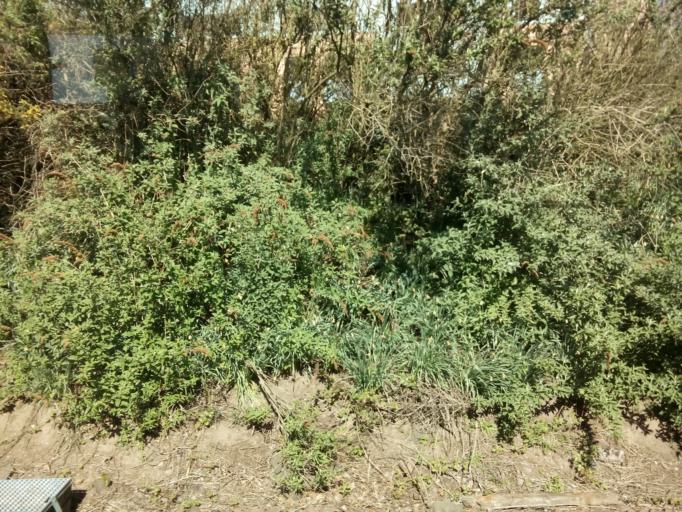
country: GB
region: Scotland
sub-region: Dundee City
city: Dundee
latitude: 56.4560
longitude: -2.9730
